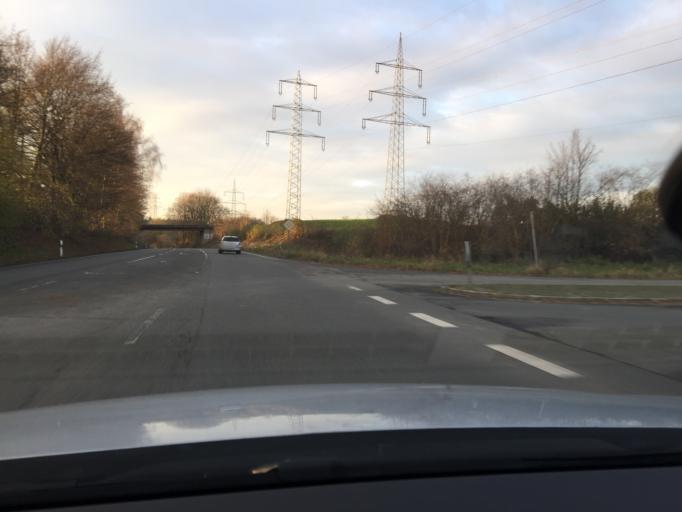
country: DE
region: North Rhine-Westphalia
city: Sprockhovel
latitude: 51.3301
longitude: 7.2264
